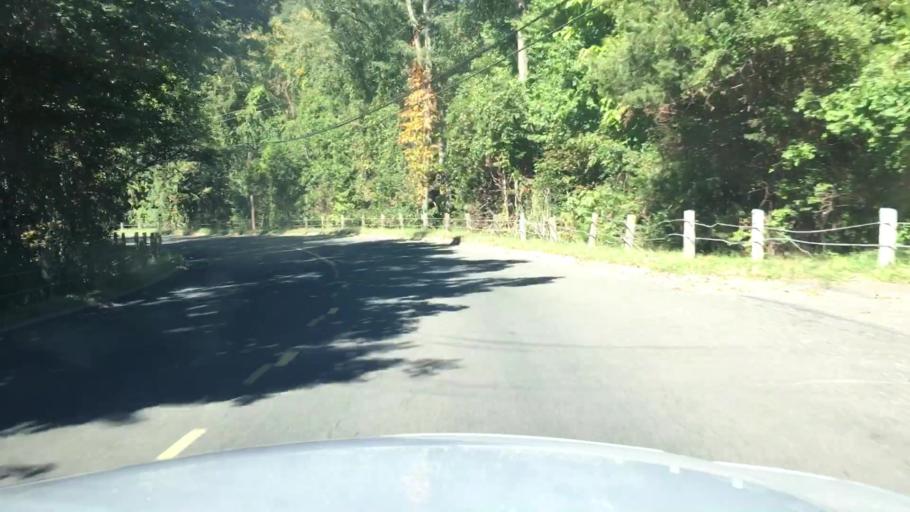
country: US
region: Connecticut
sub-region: Middlesex County
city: Essex Village
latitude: 41.3550
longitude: -72.4081
